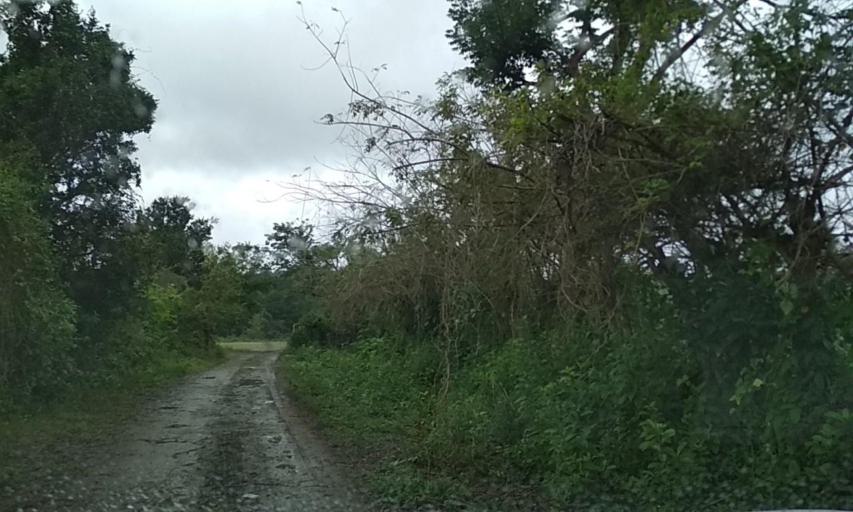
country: MX
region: Veracruz
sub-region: Papantla
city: El Chote
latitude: 20.3768
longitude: -97.3458
